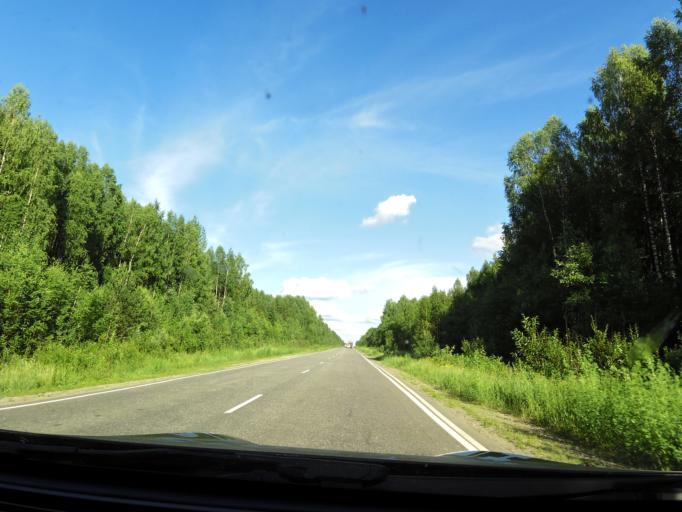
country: RU
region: Kirov
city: Chernaya Kholunitsa
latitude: 58.7714
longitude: 51.9516
